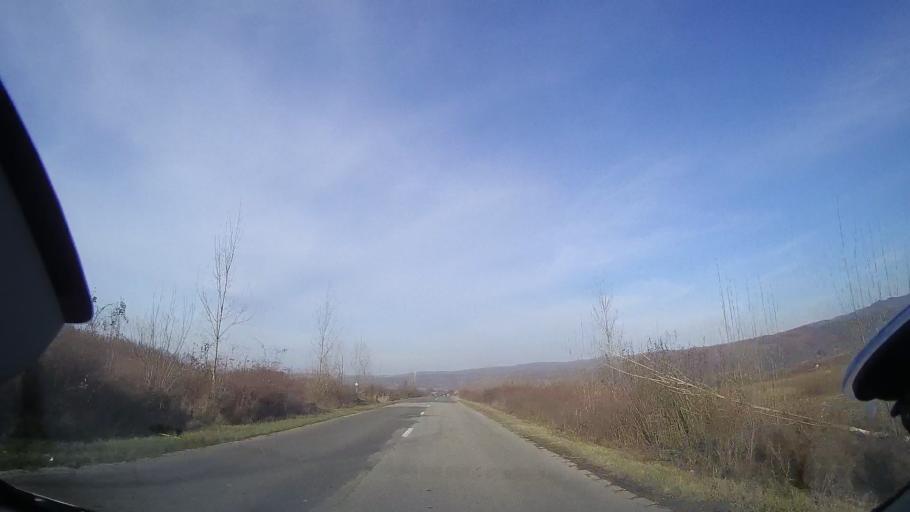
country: RO
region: Bihor
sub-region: Comuna Brusturi
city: Brusturi
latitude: 47.1214
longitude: 22.2695
